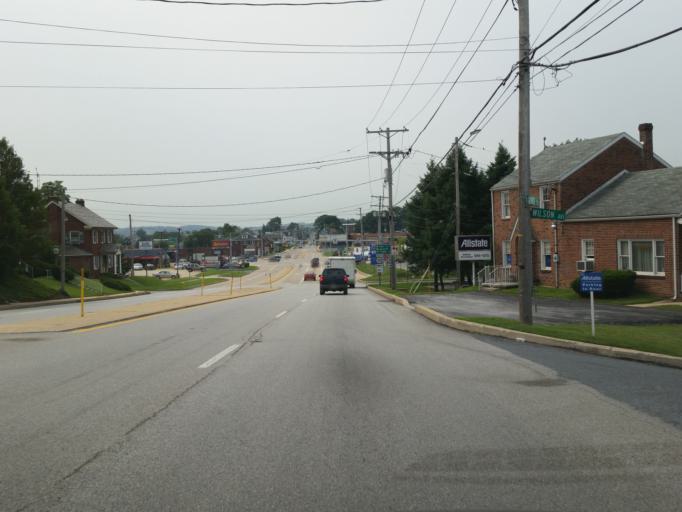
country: US
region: Pennsylvania
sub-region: York County
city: North York
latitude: 39.9859
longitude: -76.7357
